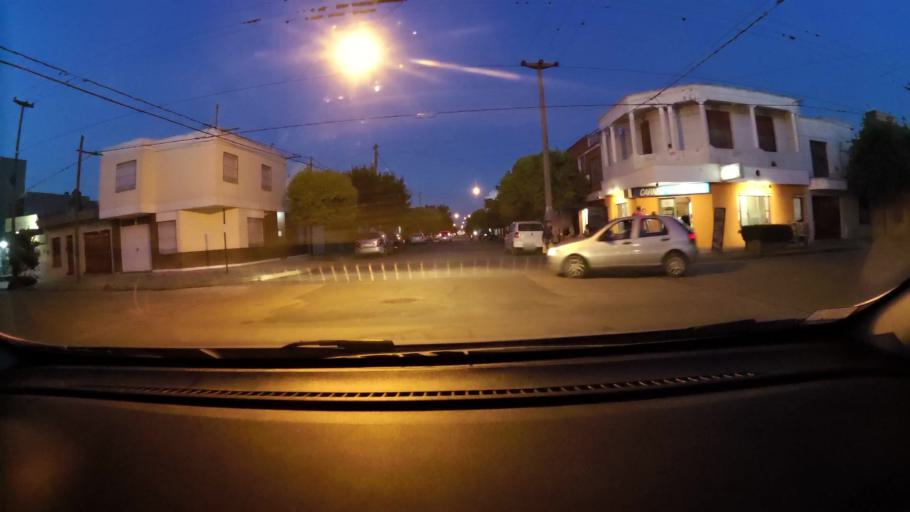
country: AR
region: Cordoba
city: Villa Maria
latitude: -32.4065
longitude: -63.2387
